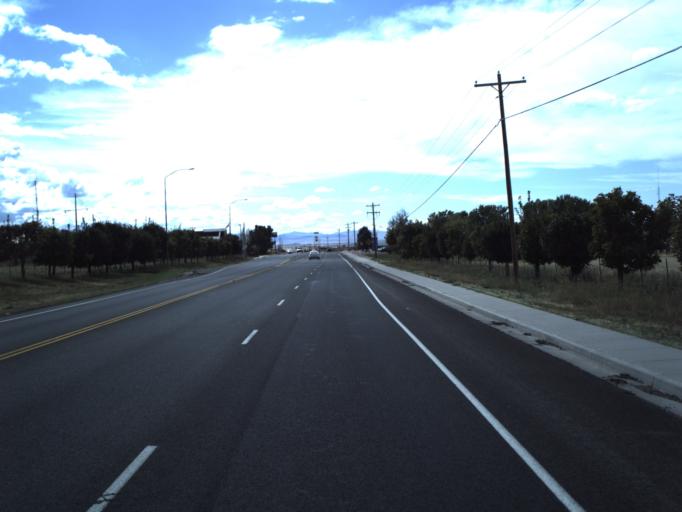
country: US
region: Utah
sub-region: Millard County
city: Fillmore
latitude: 38.9559
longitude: -112.3373
